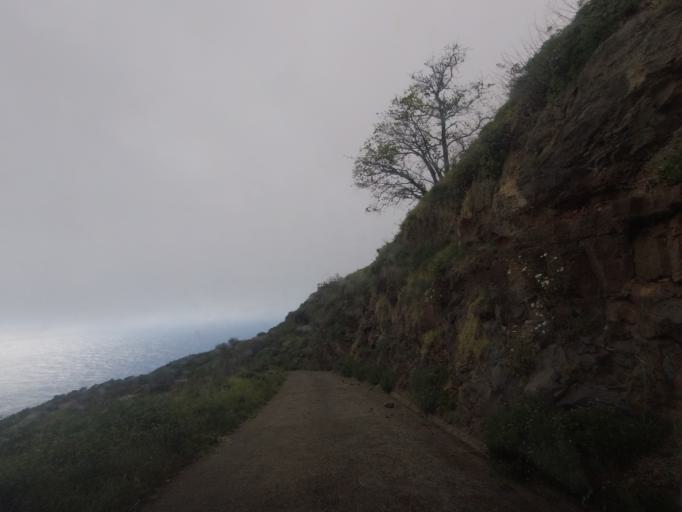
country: PT
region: Madeira
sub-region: Calheta
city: Faja da Ovelha
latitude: 32.7592
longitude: -17.2219
